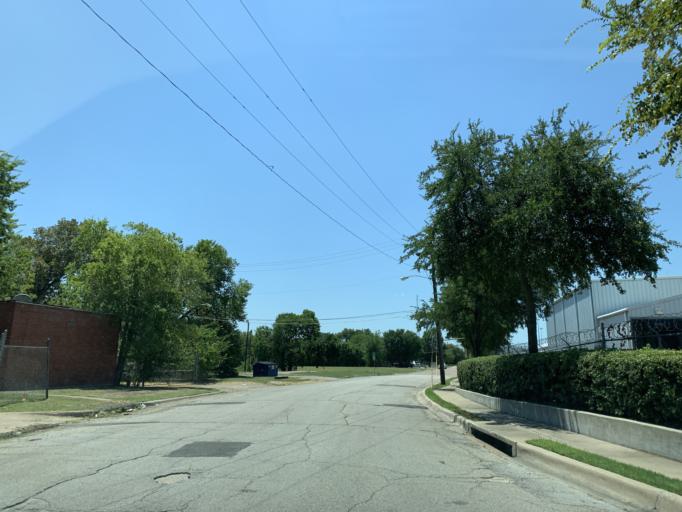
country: US
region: Texas
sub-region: Dallas County
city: Dallas
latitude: 32.7775
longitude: -96.7725
